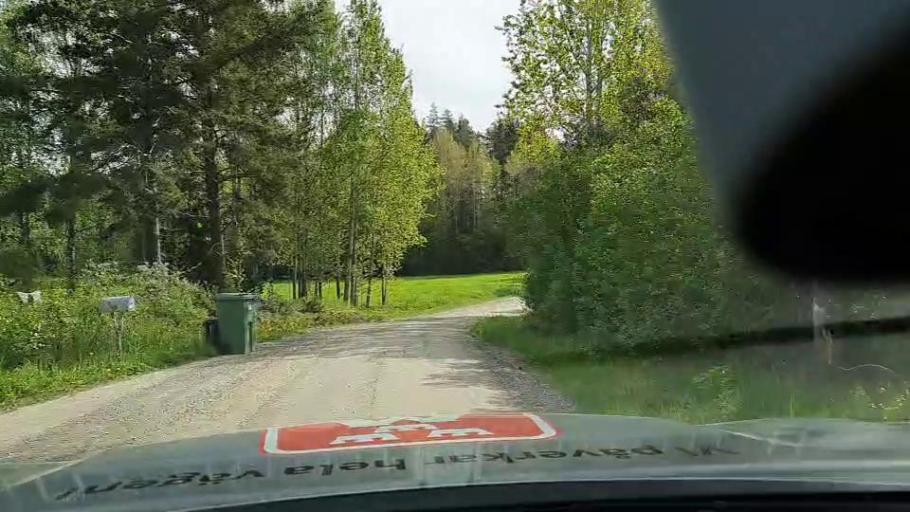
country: SE
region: Soedermanland
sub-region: Strangnas Kommun
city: Strangnas
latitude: 59.2634
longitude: 16.8898
